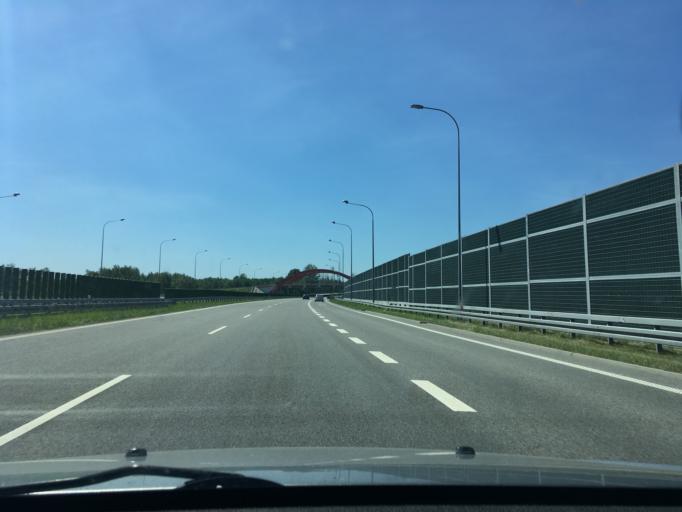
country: PL
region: Subcarpathian Voivodeship
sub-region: Powiat debicki
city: Brzeznica
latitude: 50.0799
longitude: 21.4760
